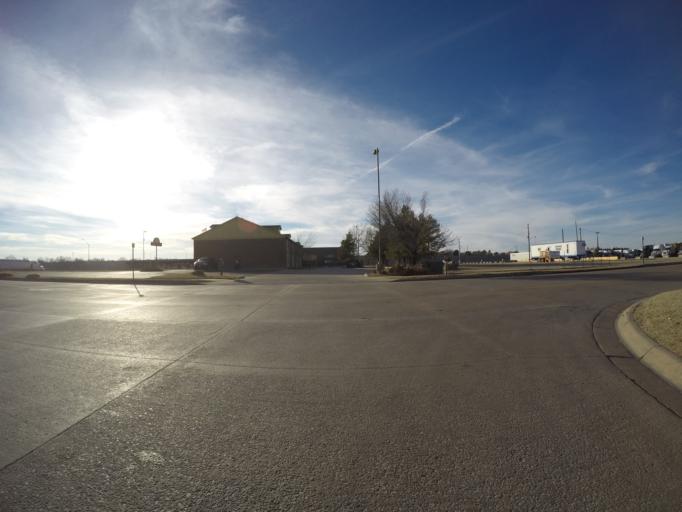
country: US
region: Kansas
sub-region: Harvey County
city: Newton
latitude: 38.0435
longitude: -97.3201
